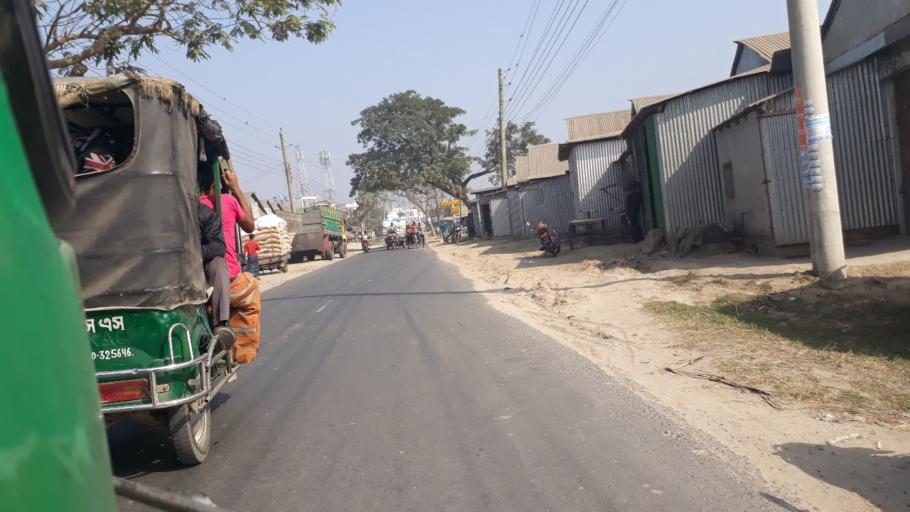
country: BD
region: Khulna
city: Kushtia
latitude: 23.8643
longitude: 89.0525
